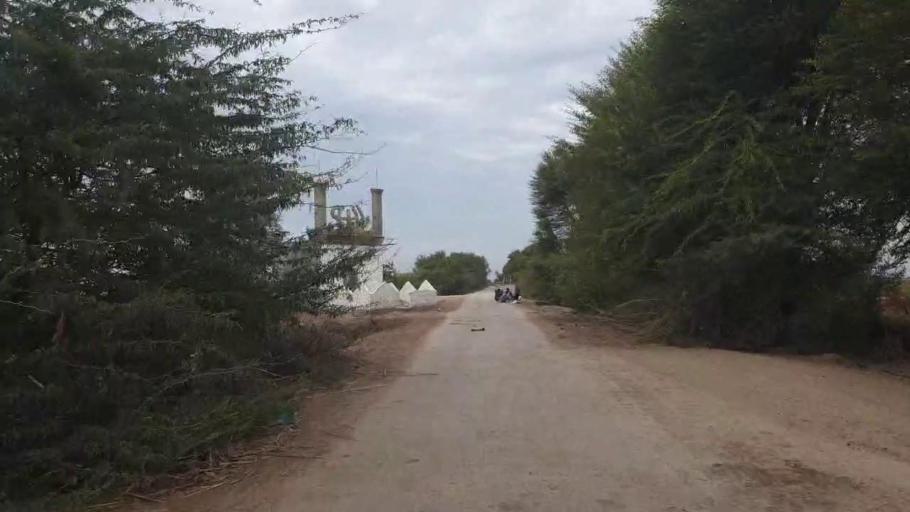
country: PK
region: Sindh
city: Jhol
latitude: 25.9957
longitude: 68.8906
